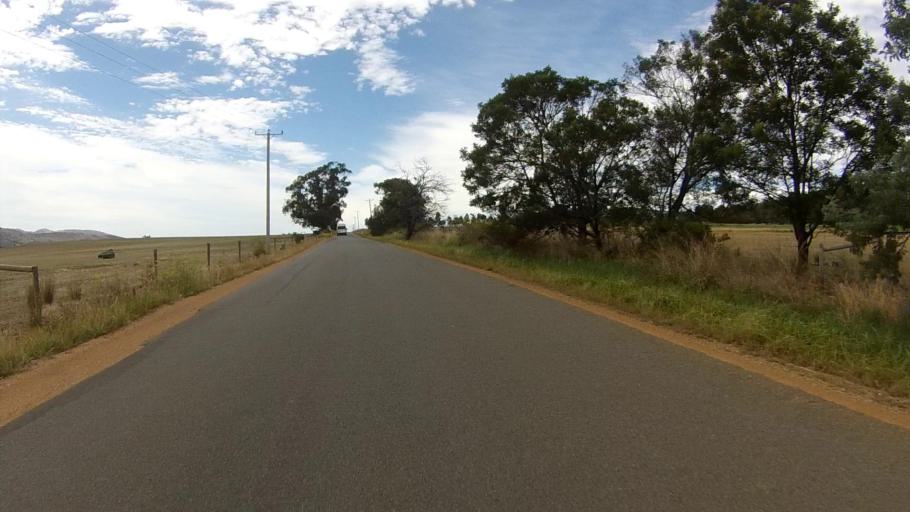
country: AU
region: Tasmania
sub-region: Clarence
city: Lindisfarne
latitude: -42.7545
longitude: 147.3795
